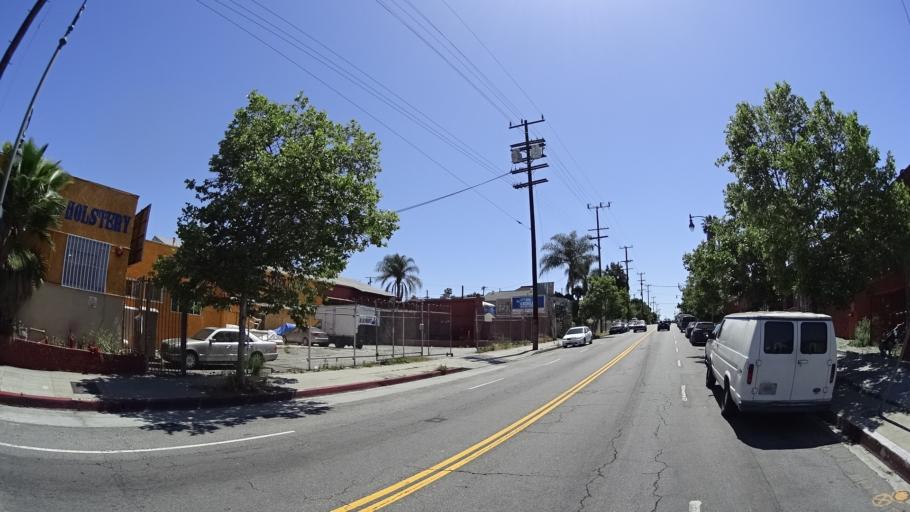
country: US
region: California
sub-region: Los Angeles County
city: Los Angeles
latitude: 34.0794
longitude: -118.2184
